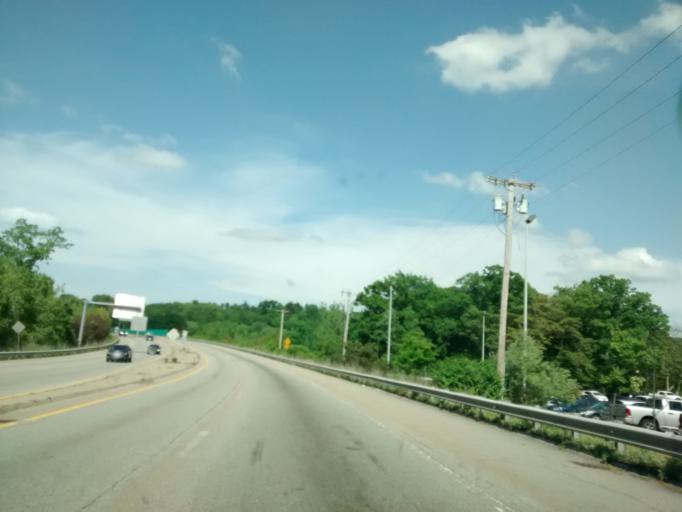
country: US
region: Massachusetts
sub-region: Worcester County
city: Millbury
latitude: 42.2107
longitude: -71.7878
